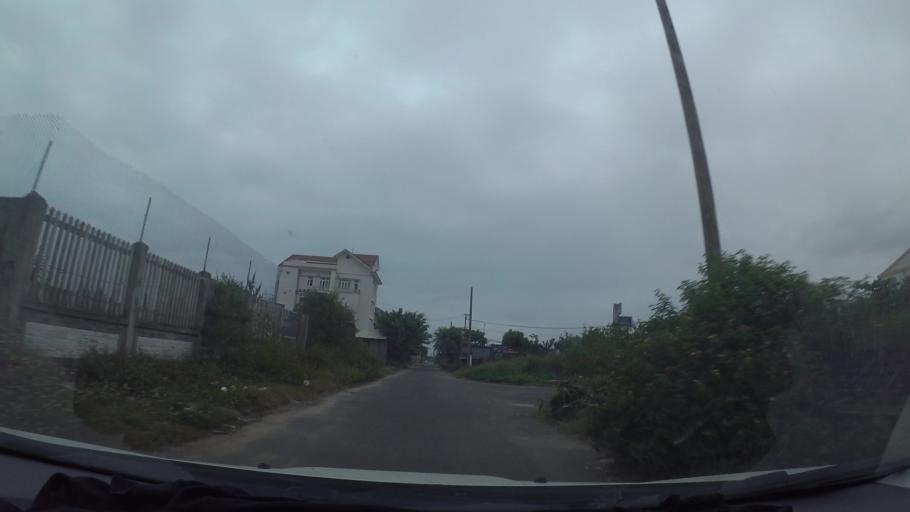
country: VN
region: Da Nang
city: Lien Chieu
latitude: 16.0886
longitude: 108.1533
